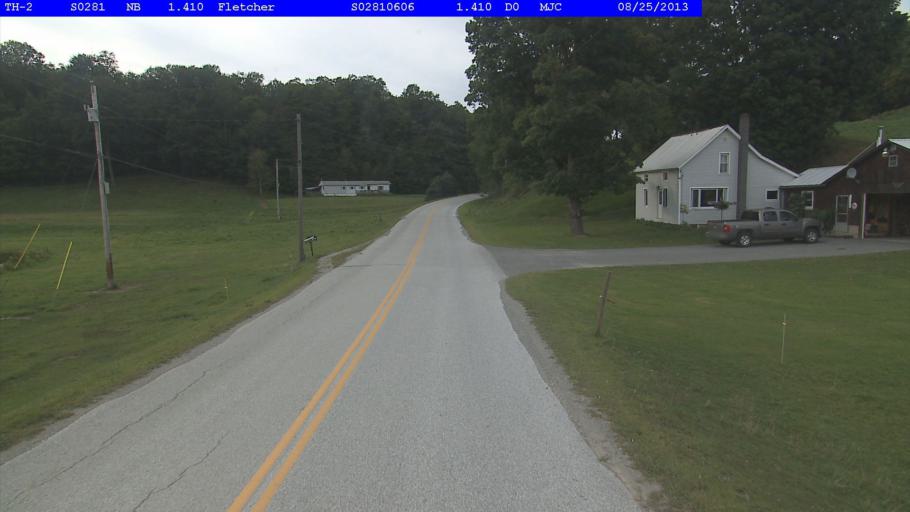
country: US
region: Vermont
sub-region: Chittenden County
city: Milton
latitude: 44.6958
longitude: -72.9342
